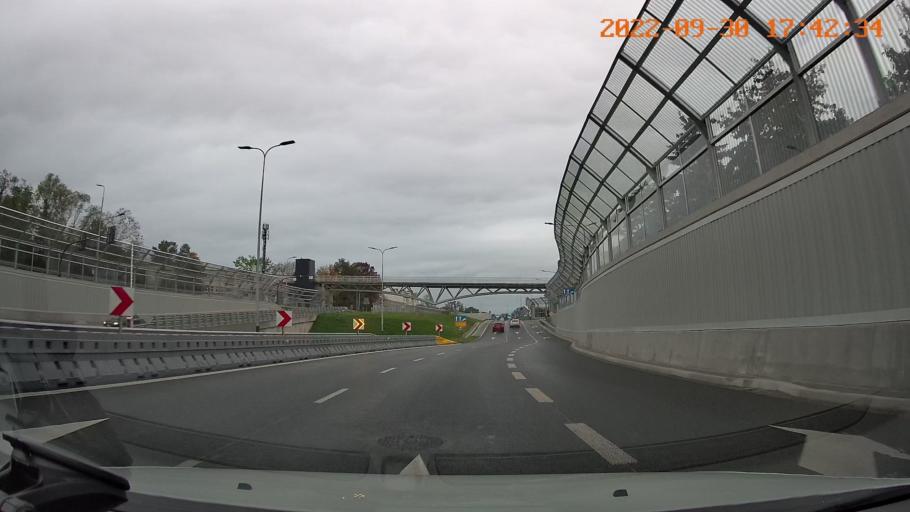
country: PL
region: Lesser Poland Voivodeship
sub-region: Krakow
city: Krakow
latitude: 50.0256
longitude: 19.9179
